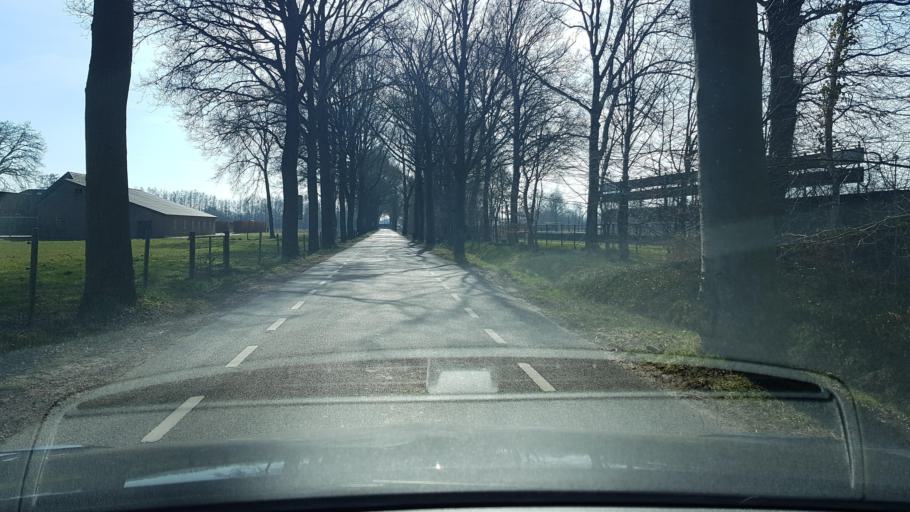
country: NL
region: Gelderland
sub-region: Gemeente Epe
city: Emst
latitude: 52.3148
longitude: 5.9529
